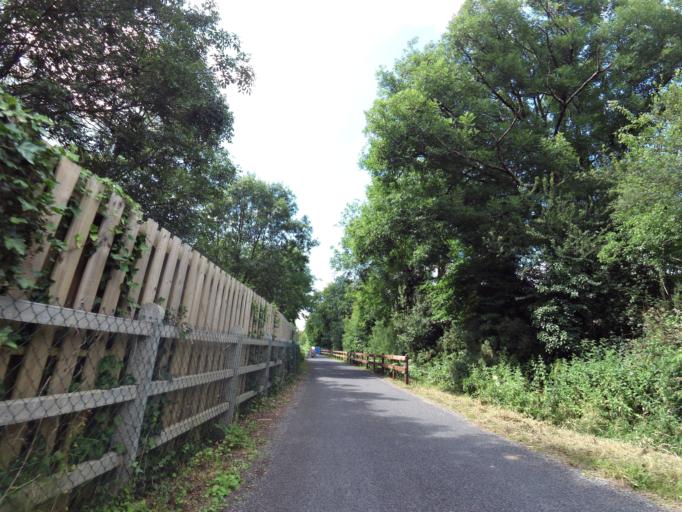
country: IE
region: Munster
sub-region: Waterford
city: Portlaw
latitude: 52.2382
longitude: -7.2939
